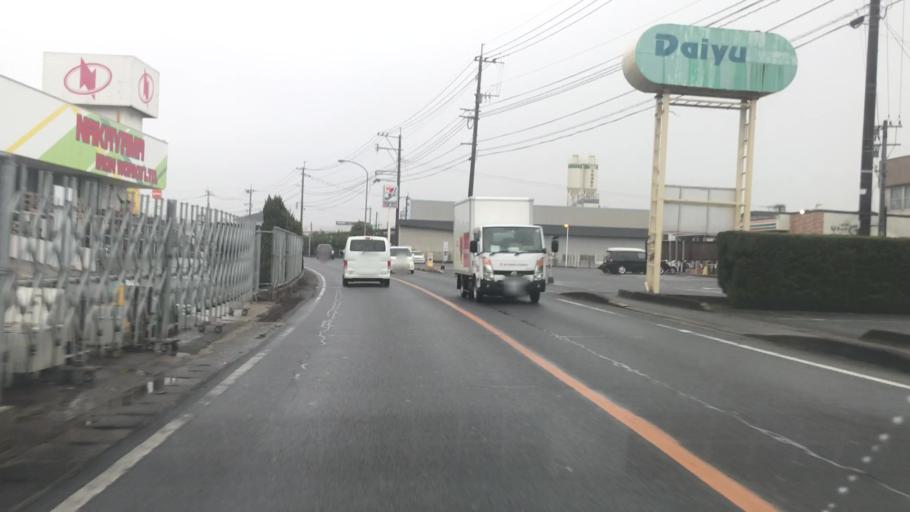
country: JP
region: Saga Prefecture
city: Takeocho-takeo
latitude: 33.2113
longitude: 130.0468
